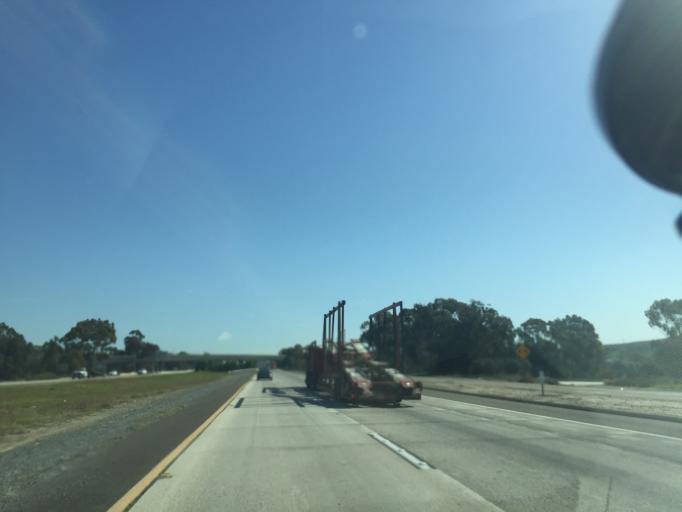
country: US
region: California
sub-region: San Diego County
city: Imperial Beach
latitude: 32.5681
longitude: -117.0437
